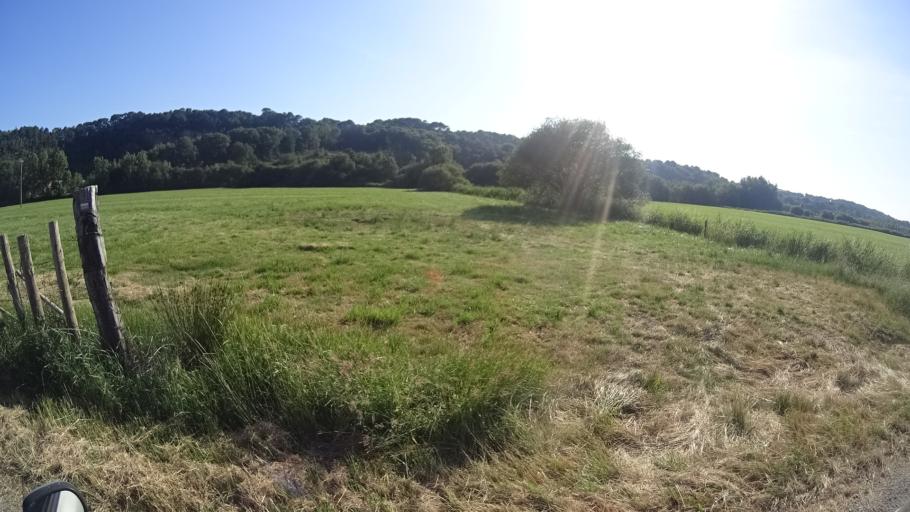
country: FR
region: Brittany
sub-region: Departement du Morbihan
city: Saint-Jean-la-Poterie
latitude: 47.6388
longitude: -2.1058
